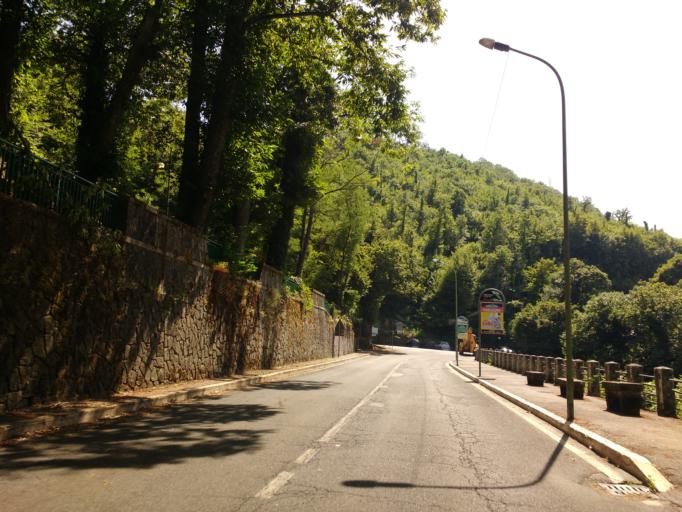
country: IT
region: Latium
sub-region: Citta metropolitana di Roma Capitale
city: Rocca di Papa
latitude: 41.7549
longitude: 12.7058
